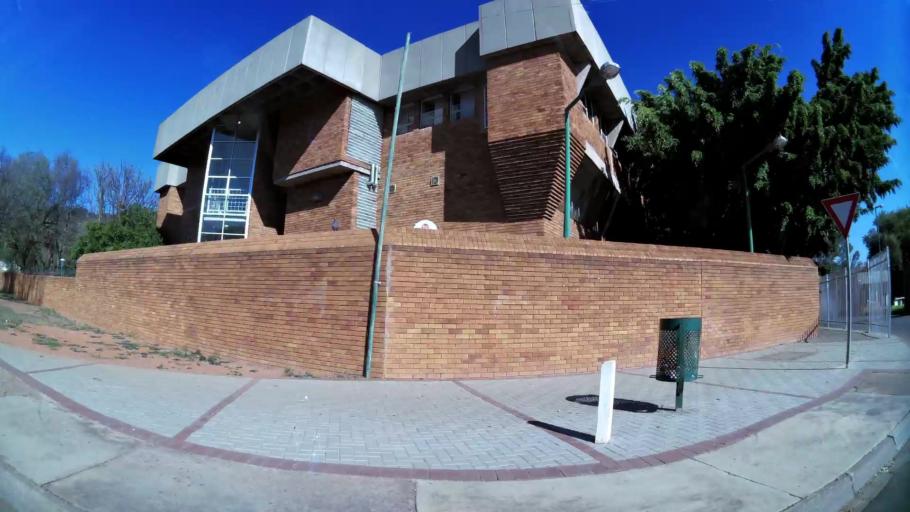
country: ZA
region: Gauteng
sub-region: City of Tshwane Metropolitan Municipality
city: Pretoria
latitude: -25.7697
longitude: 28.2098
